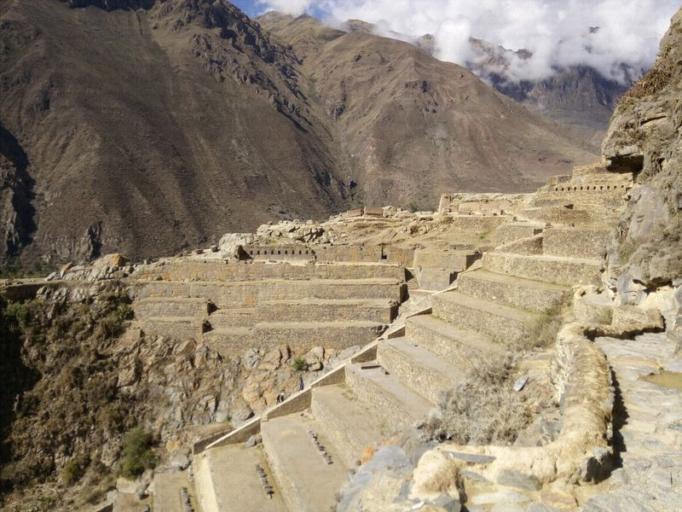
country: PE
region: Cusco
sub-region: Provincia de Urubamba
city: Ollantaytambo
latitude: -13.2597
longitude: -72.2673
